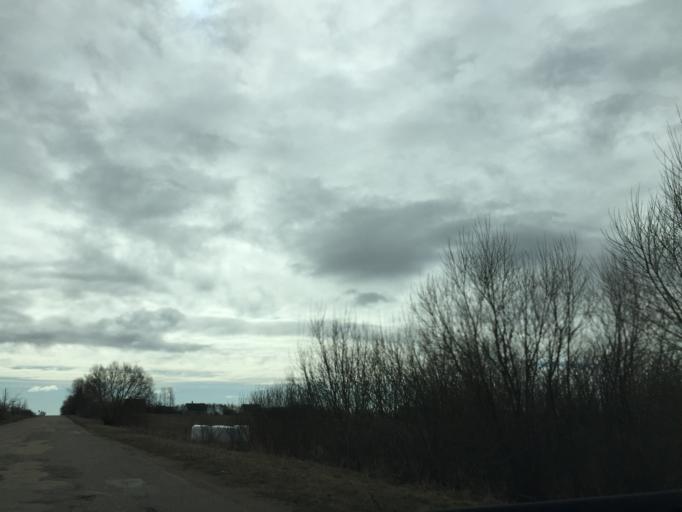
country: LV
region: Daugavpils
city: Daugavpils
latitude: 55.9221
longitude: 26.7394
